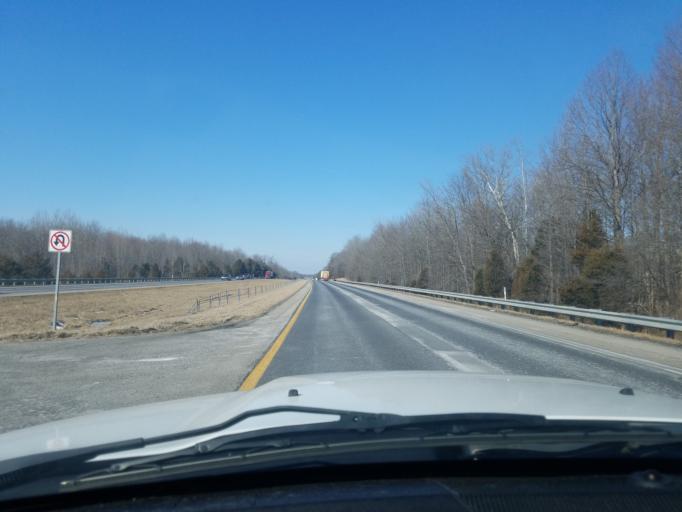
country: US
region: Indiana
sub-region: Bartholomew County
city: Columbus
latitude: 39.0835
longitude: -85.9323
